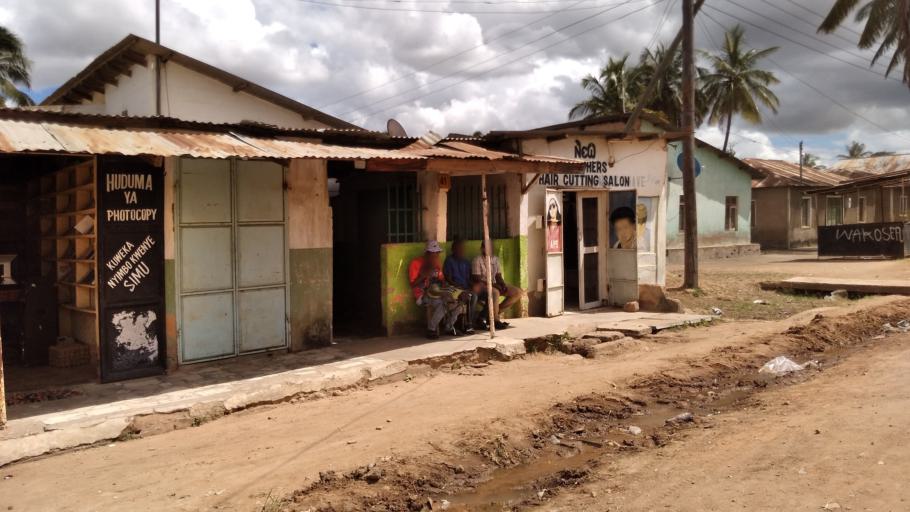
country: TZ
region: Dodoma
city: Dodoma
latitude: -6.1658
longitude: 35.7384
